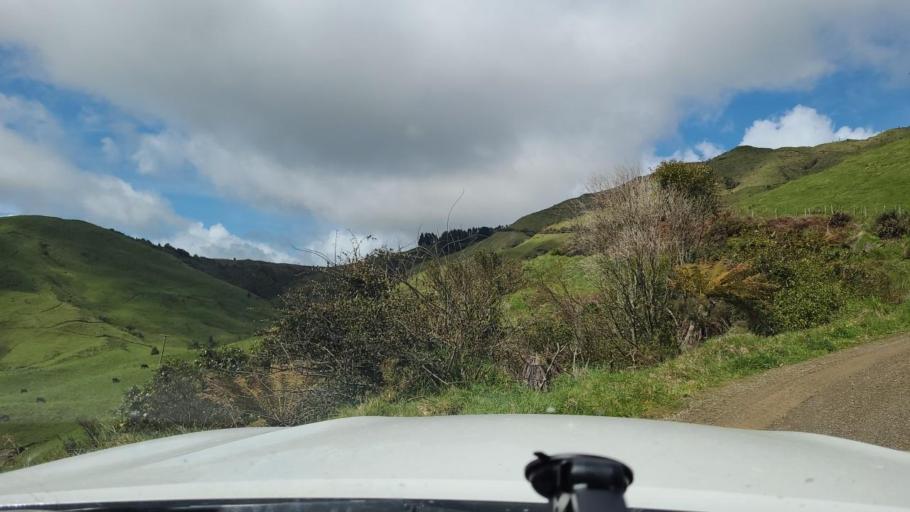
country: NZ
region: Bay of Plenty
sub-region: Opotiki District
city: Opotiki
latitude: -38.2764
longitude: 177.5710
